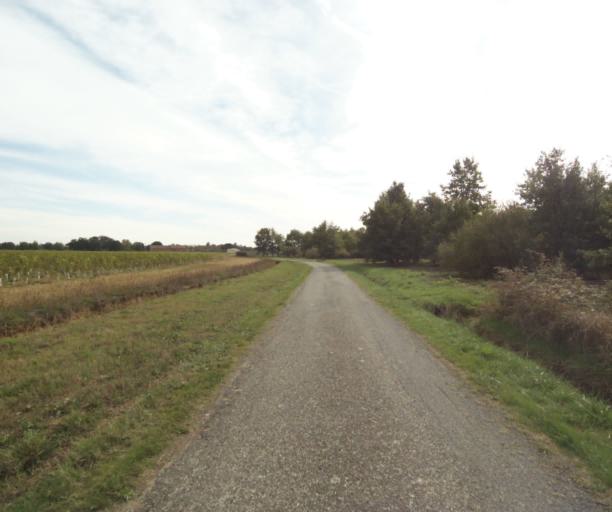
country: FR
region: Midi-Pyrenees
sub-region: Departement de la Haute-Garonne
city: Fronton
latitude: 43.8727
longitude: 1.3823
